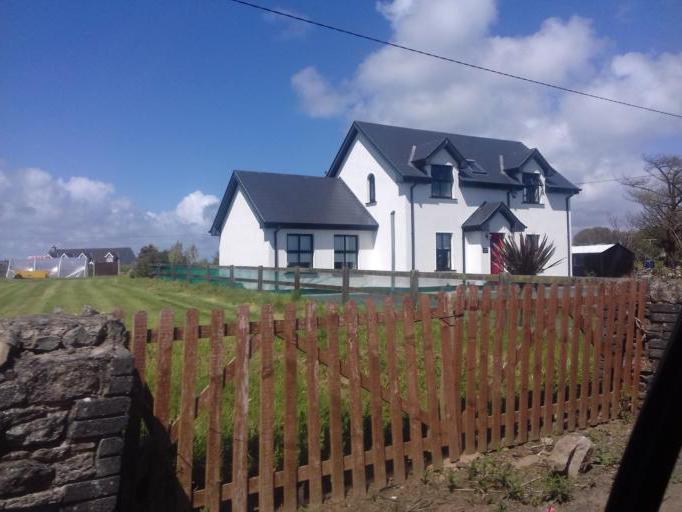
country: IE
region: Munster
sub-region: Waterford
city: Dunmore East
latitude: 52.1350
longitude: -6.9250
